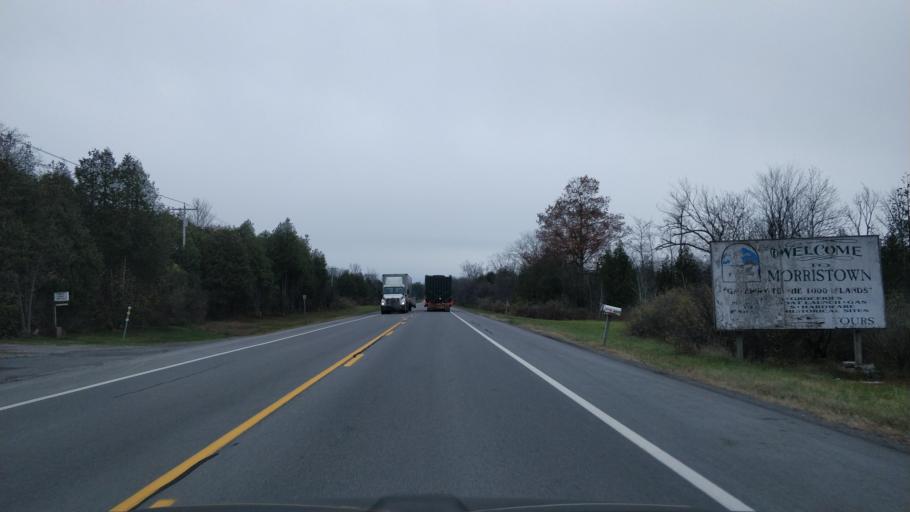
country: CA
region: Ontario
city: Brockville
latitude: 44.6088
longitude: -75.6115
